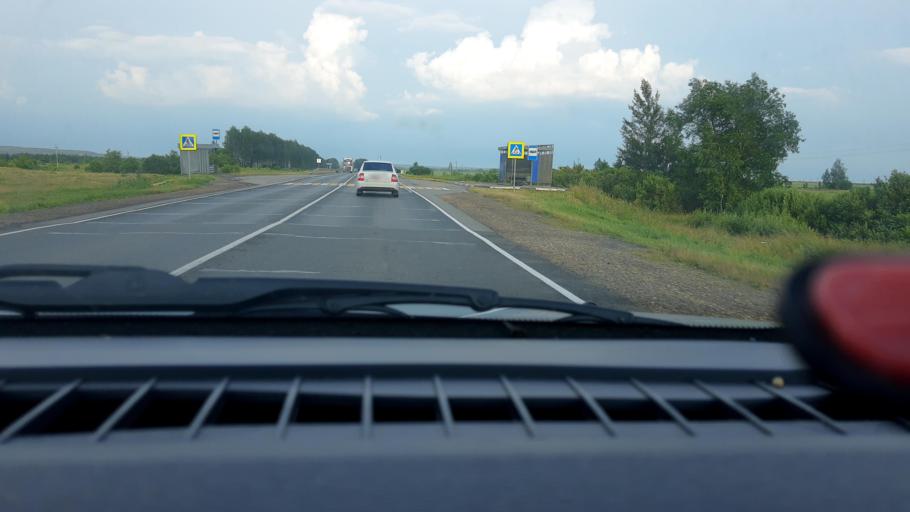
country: RU
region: Nizjnij Novgorod
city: Shatki
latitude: 55.2456
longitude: 44.0080
